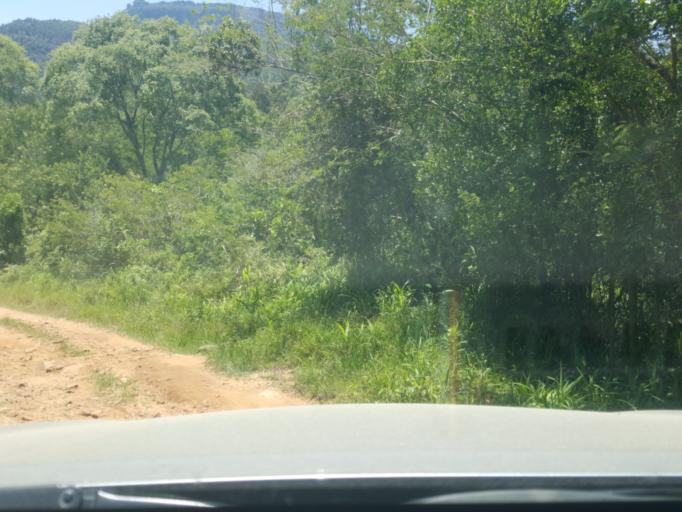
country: ZA
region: Limpopo
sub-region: Mopani District Municipality
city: Hoedspruit
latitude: -24.5963
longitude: 30.8670
